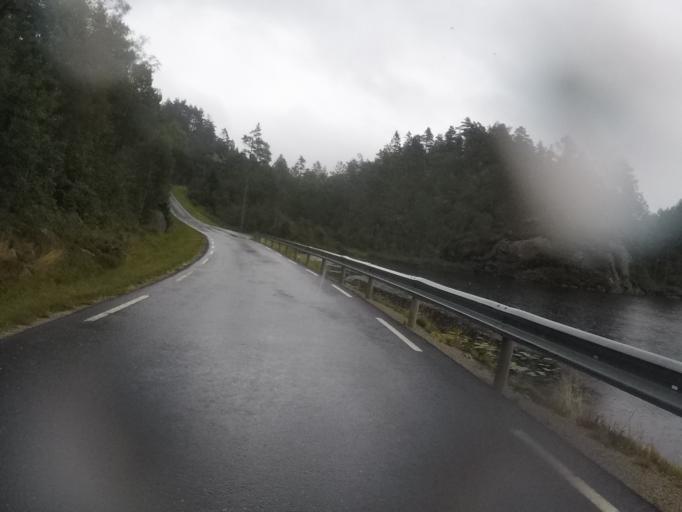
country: NO
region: Vest-Agder
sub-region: Lyngdal
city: Lyngdal
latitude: 58.2465
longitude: 7.1128
